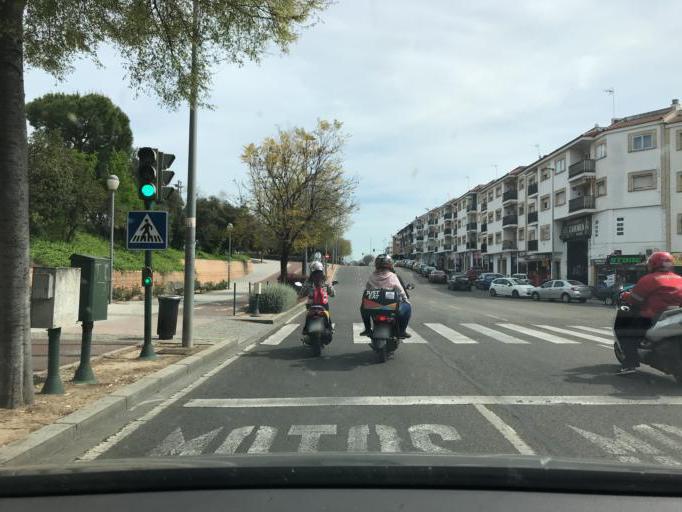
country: ES
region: Andalusia
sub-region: Province of Cordoba
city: Cordoba
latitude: 37.8948
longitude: -4.7751
